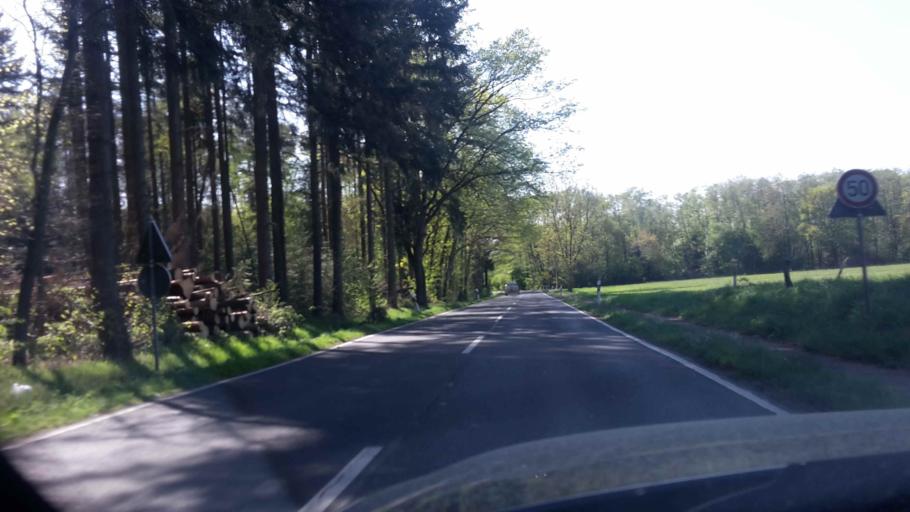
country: DE
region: North Rhine-Westphalia
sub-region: Regierungsbezirk Koln
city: Hennef
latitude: 50.7069
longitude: 7.3148
